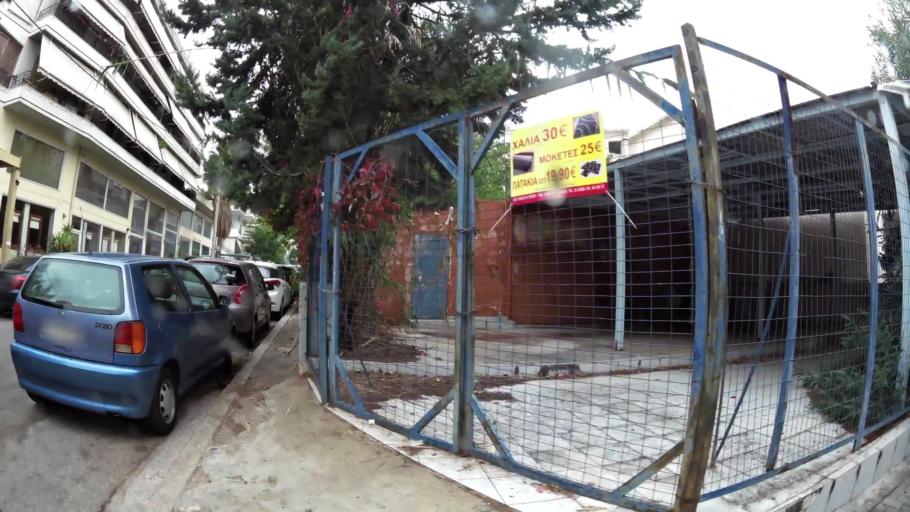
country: GR
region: Attica
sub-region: Nomarchia Athinas
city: Chaidari
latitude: 38.0079
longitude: 23.6648
